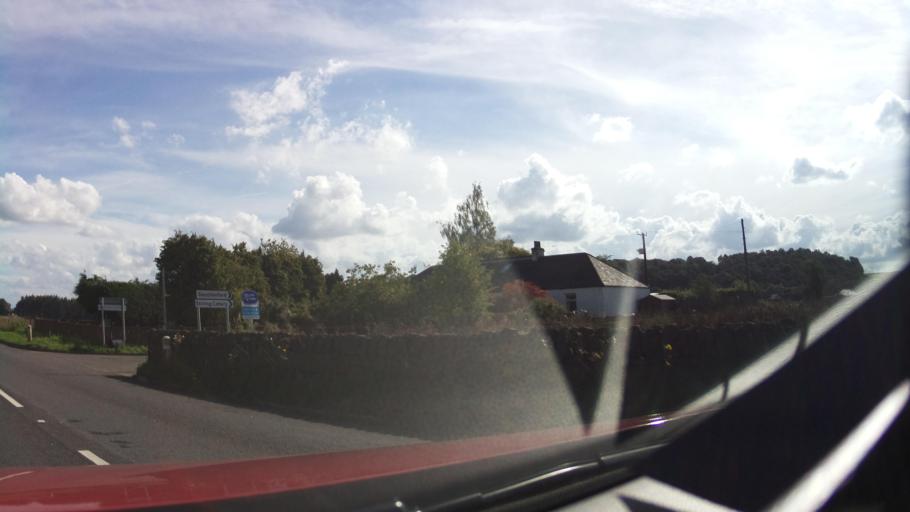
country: GB
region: Scotland
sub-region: Stirling
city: Plean
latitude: 56.0741
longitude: -3.8867
